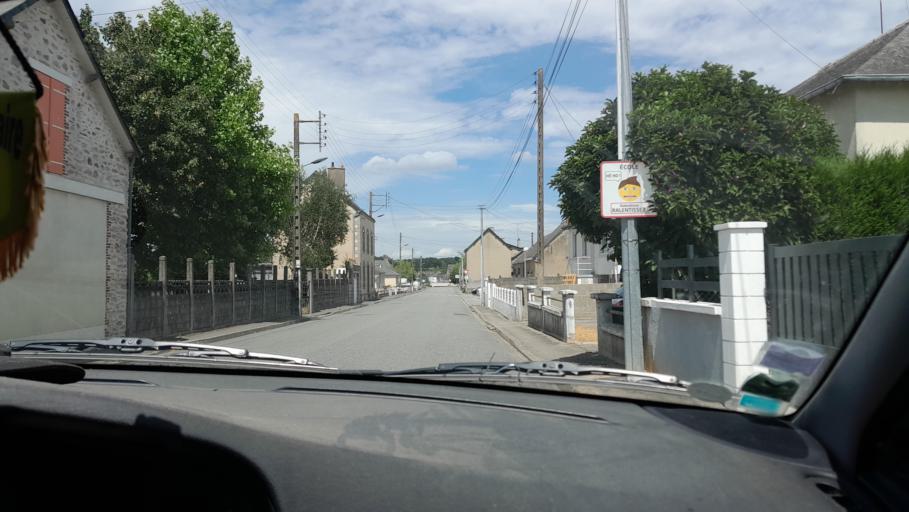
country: FR
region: Pays de la Loire
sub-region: Departement de la Mayenne
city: Saint-Pierre-la-Cour
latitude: 48.1109
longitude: -1.0245
